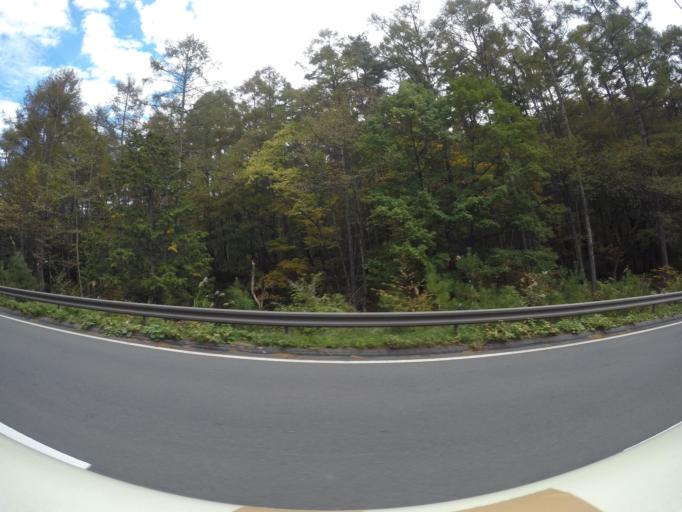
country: JP
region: Nagano
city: Chino
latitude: 35.9590
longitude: 138.1123
